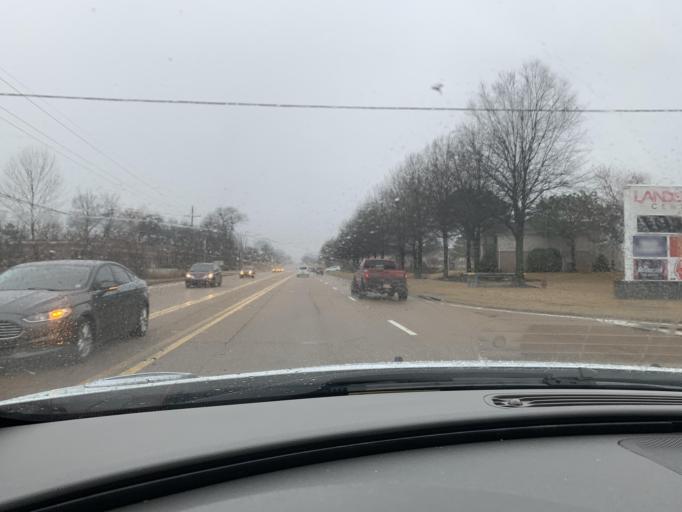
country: US
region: Mississippi
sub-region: De Soto County
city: Horn Lake
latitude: 34.9281
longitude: -90.0110
